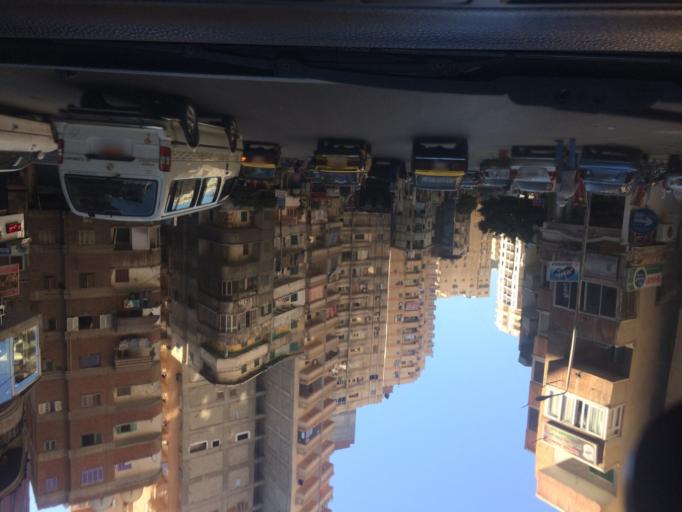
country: EG
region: Alexandria
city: Alexandria
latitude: 31.2544
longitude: 29.9842
